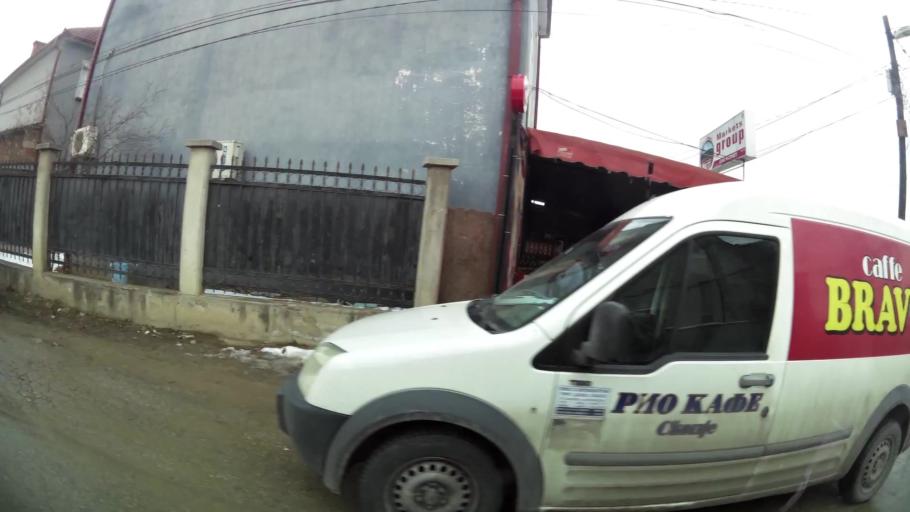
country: MK
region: Butel
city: Butel
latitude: 42.0306
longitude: 21.4342
